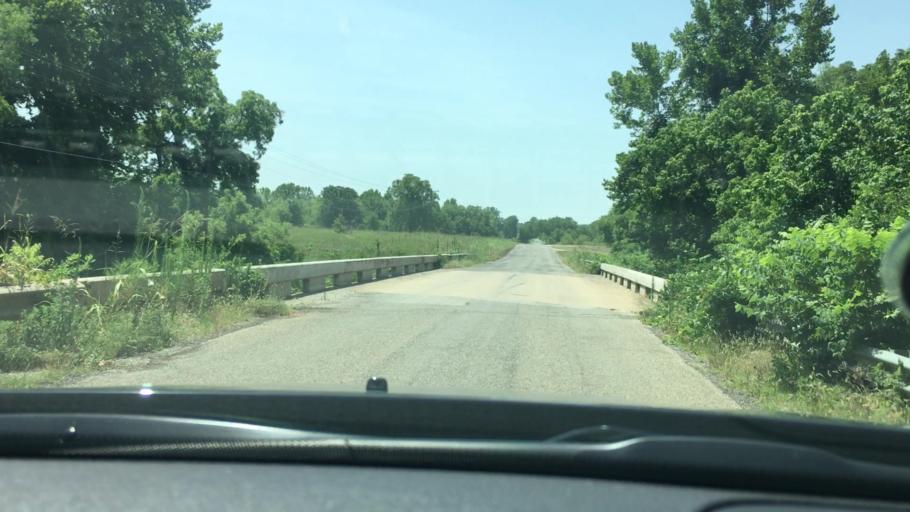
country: US
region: Oklahoma
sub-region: Pontotoc County
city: Byng
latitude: 34.8398
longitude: -96.6698
